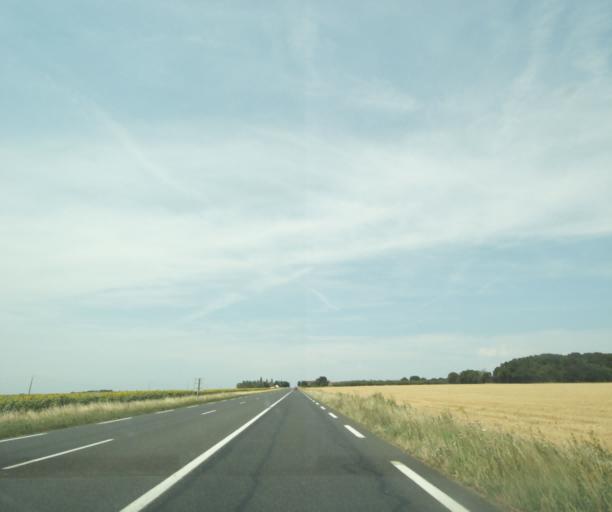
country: FR
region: Centre
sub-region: Departement d'Indre-et-Loire
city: Sainte-Maure-de-Touraine
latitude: 47.1670
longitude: 0.6517
